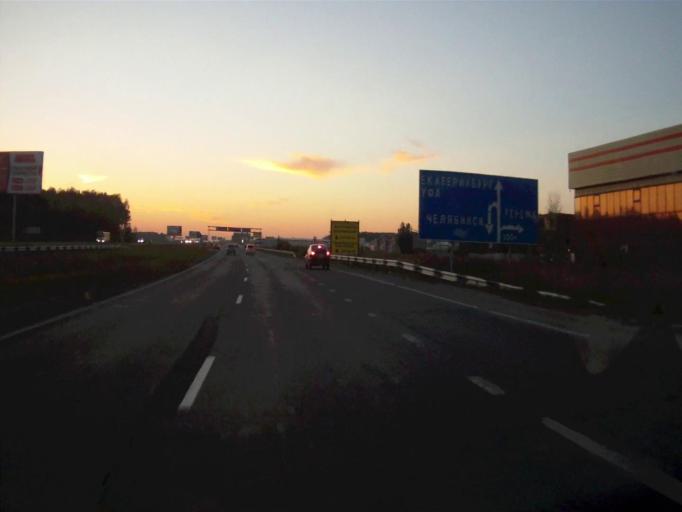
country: RU
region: Chelyabinsk
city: Roshchino
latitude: 55.1832
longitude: 61.2466
